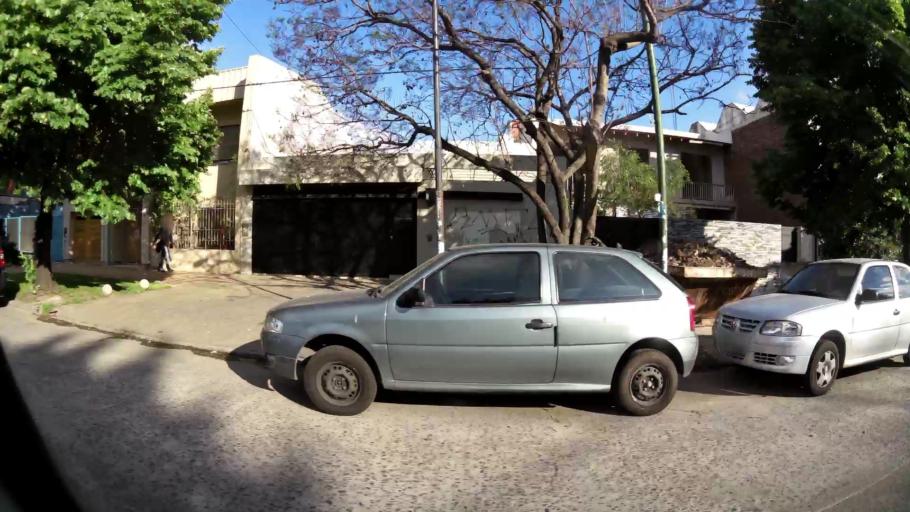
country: AR
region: Buenos Aires
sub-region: Partido de La Plata
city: La Plata
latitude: -34.8972
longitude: -57.9652
